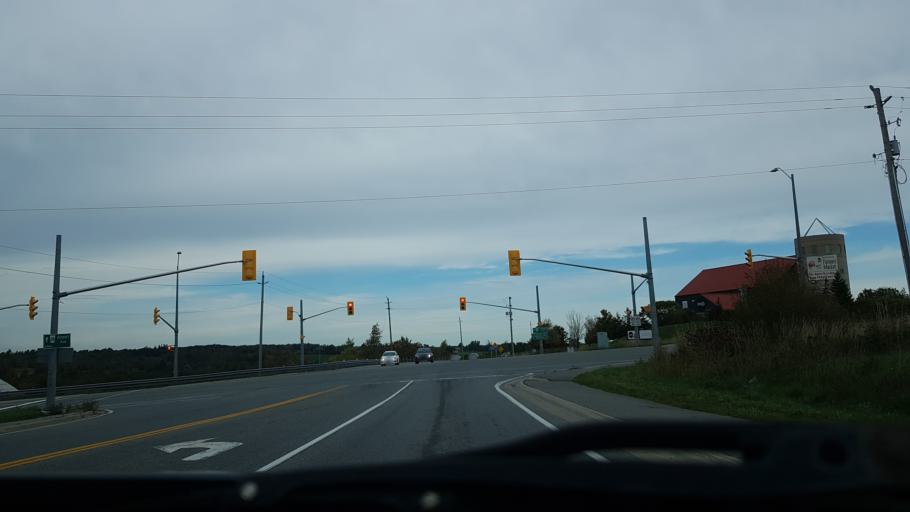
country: CA
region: Ontario
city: Shelburne
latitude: 44.1150
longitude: -80.0269
